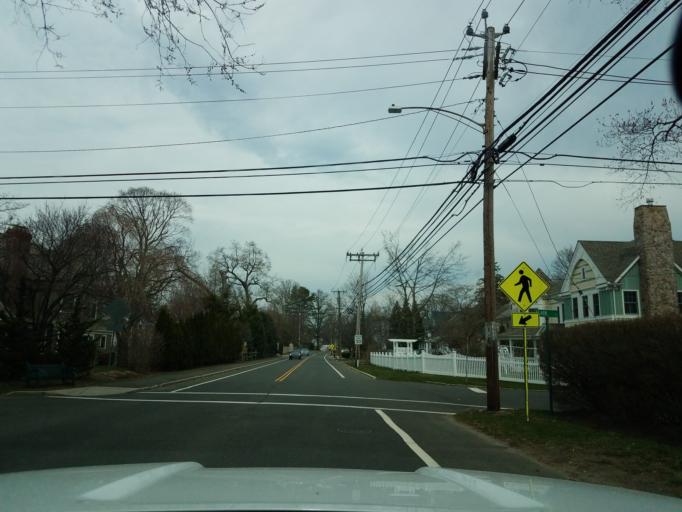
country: US
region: Connecticut
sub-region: Fairfield County
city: Old Greenwich
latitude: 41.0220
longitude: -73.5641
